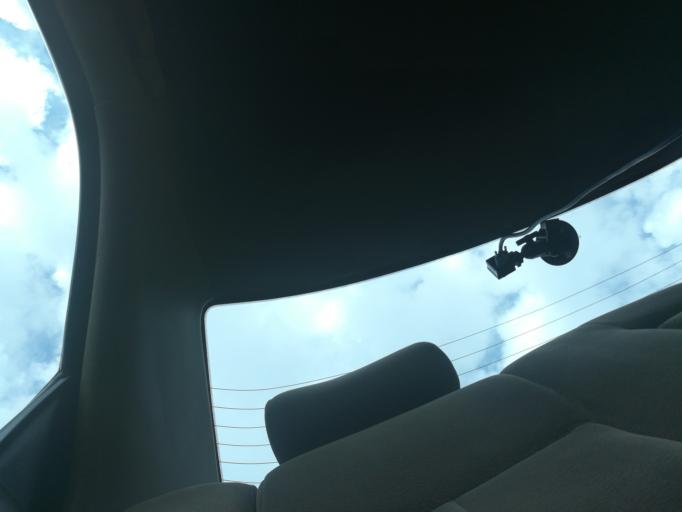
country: NG
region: Lagos
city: Ikorodu
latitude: 6.6604
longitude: 3.5885
